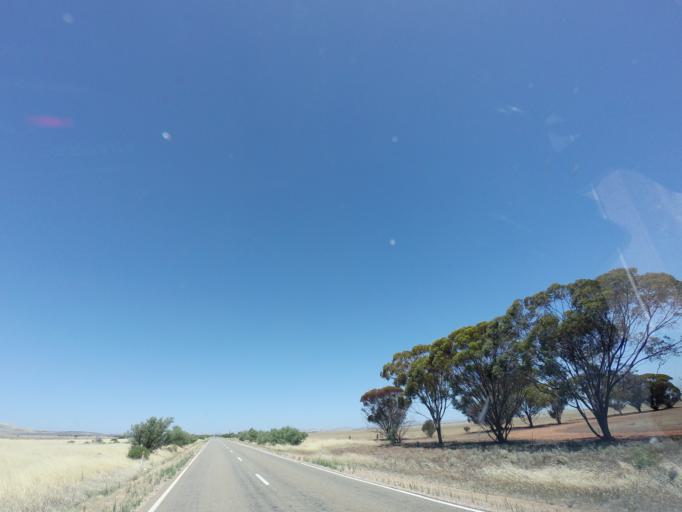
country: AU
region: South Australia
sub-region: Flinders Ranges
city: Quorn
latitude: -32.6884
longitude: 138.3353
